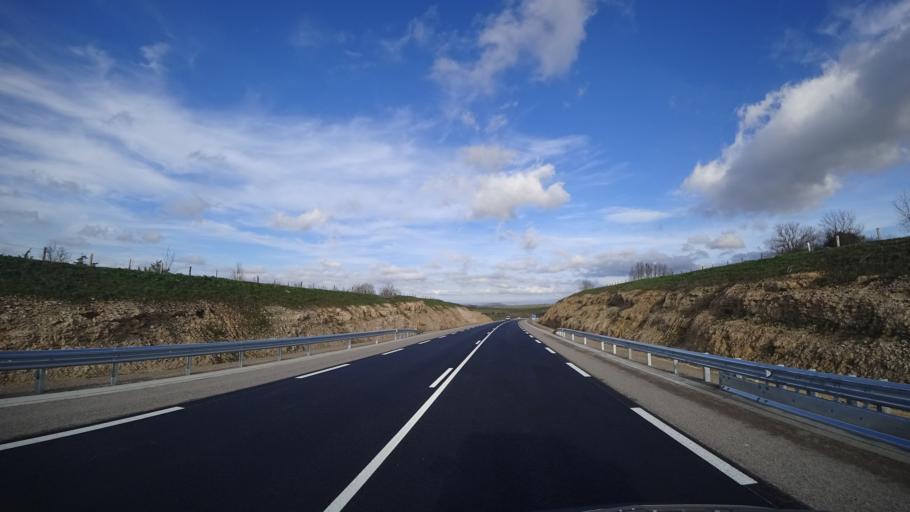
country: FR
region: Midi-Pyrenees
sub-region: Departement de l'Aveyron
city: Sebazac-Concoures
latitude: 44.4075
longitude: 2.6232
